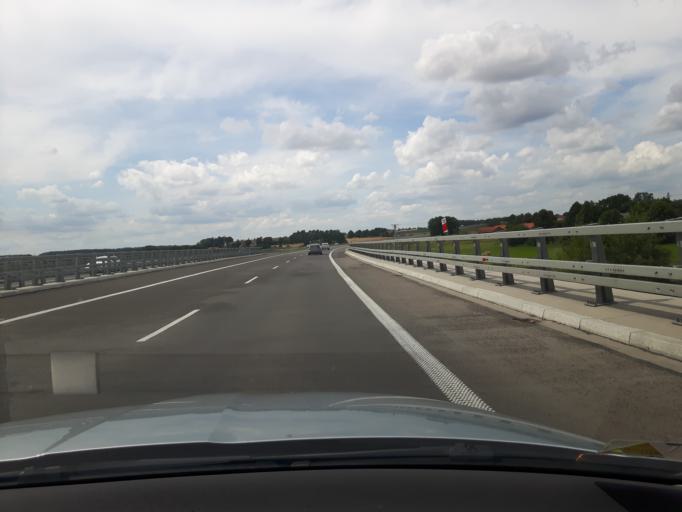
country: PL
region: Warmian-Masurian Voivodeship
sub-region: Powiat nidzicki
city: Nidzica
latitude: 53.3409
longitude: 20.4085
